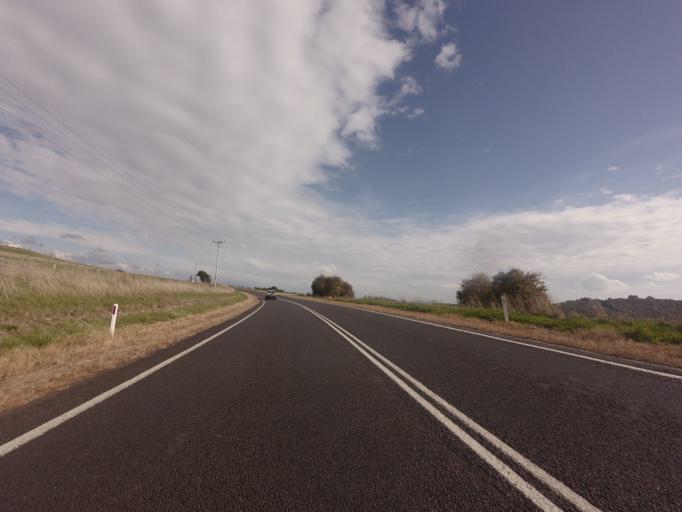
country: AU
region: Tasmania
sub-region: Meander Valley
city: Deloraine
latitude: -41.5182
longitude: 146.7233
